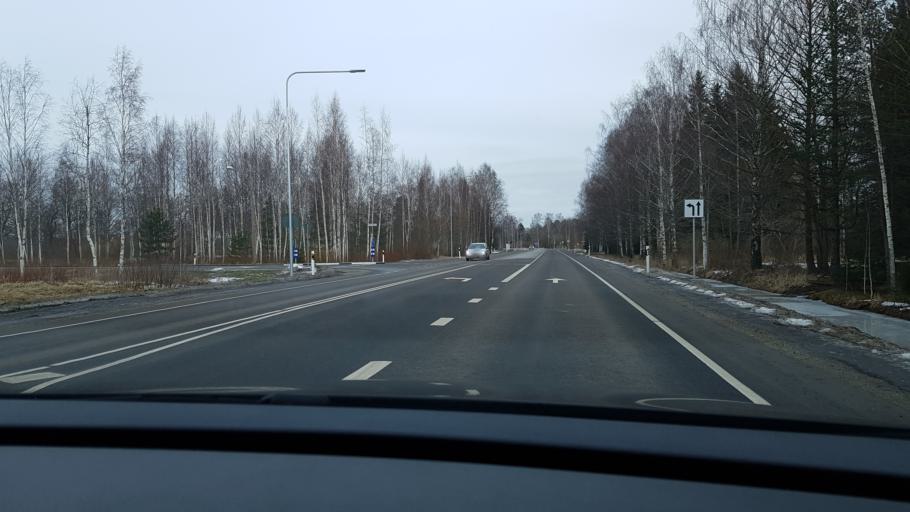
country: EE
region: Paernumaa
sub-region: Sindi linn
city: Sindi
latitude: 58.4047
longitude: 24.6616
